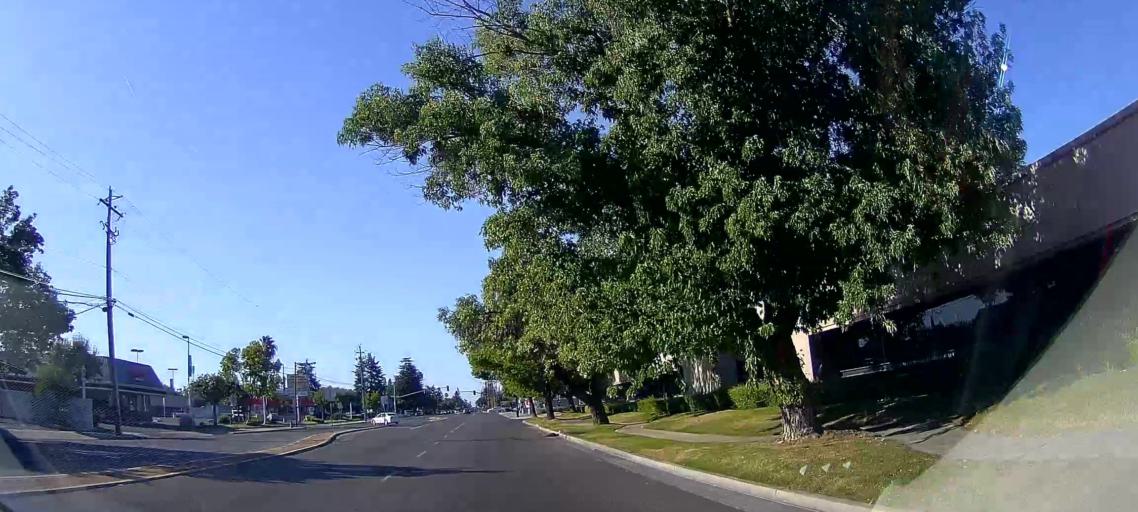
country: US
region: California
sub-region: Fresno County
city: Fresno
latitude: 36.8211
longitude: -119.8082
